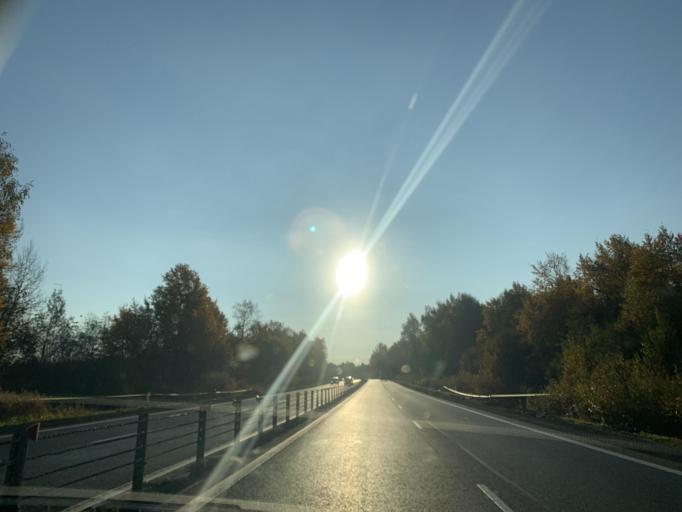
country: RU
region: Jaroslavl
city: Konstantinovskiy
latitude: 57.7810
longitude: 39.6314
